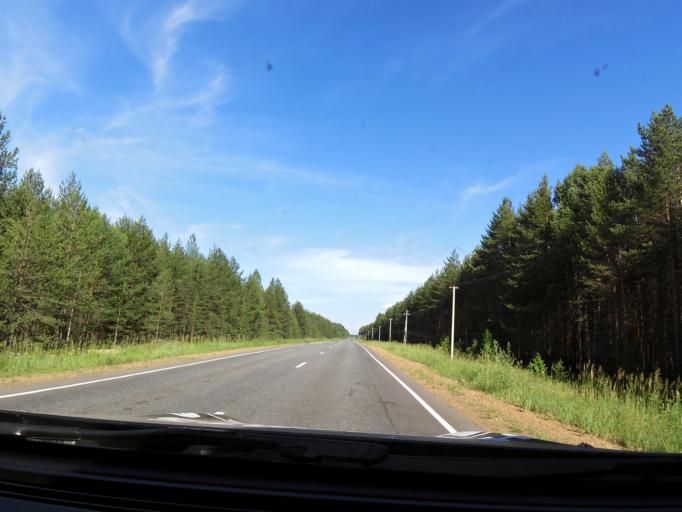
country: RU
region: Kirov
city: Belaya Kholunitsa
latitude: 58.9073
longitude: 51.0055
